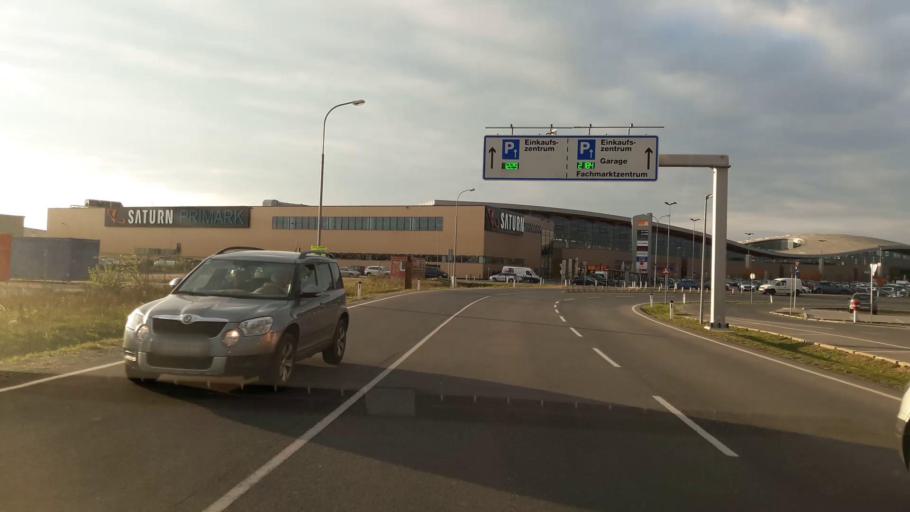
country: AT
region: Lower Austria
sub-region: Politischer Bezirk Mistelbach
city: Grossebersdorf
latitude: 48.3408
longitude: 16.4656
